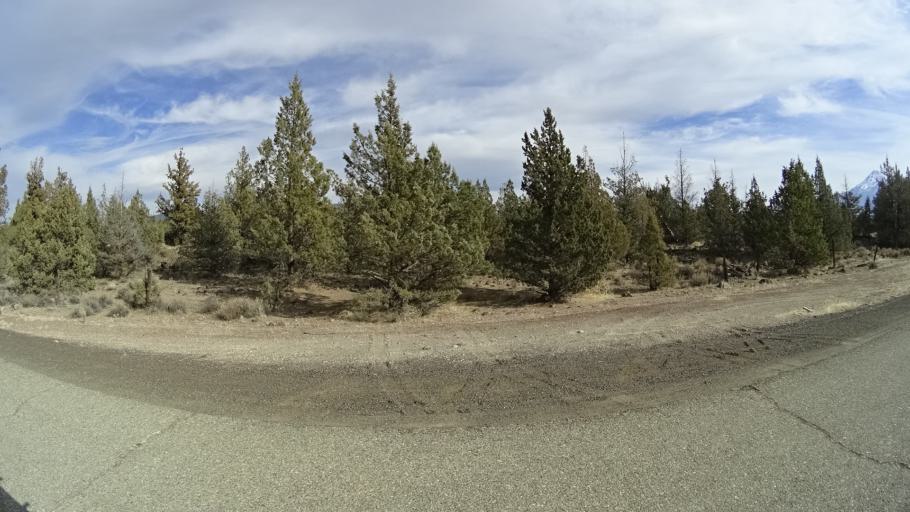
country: US
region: California
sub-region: Siskiyou County
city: Weed
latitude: 41.5915
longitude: -122.4008
